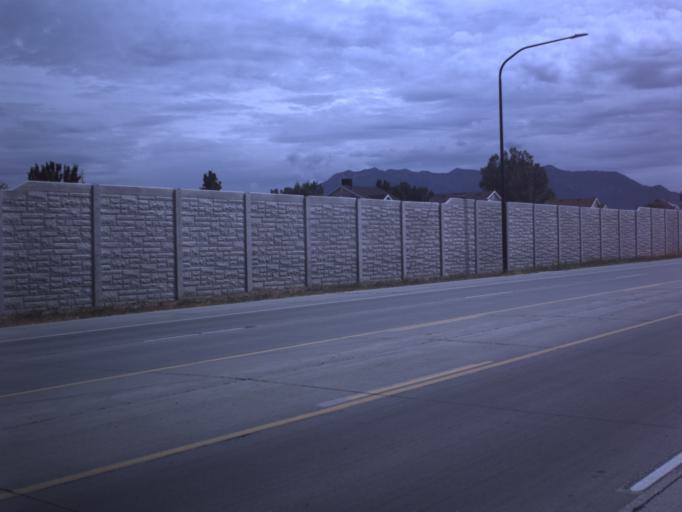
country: US
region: Utah
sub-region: Davis County
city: Clearfield
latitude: 41.1106
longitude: -112.0498
